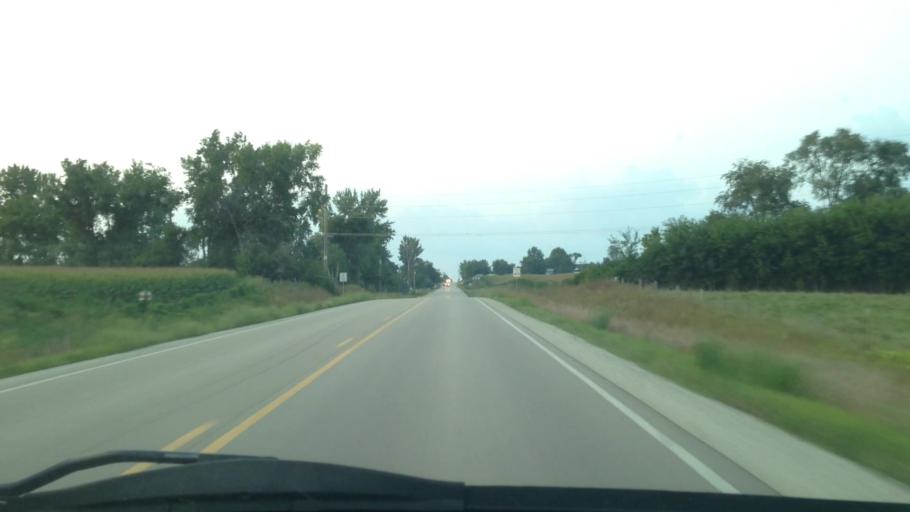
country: US
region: Iowa
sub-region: Benton County
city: Urbana
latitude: 42.2174
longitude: -91.8714
